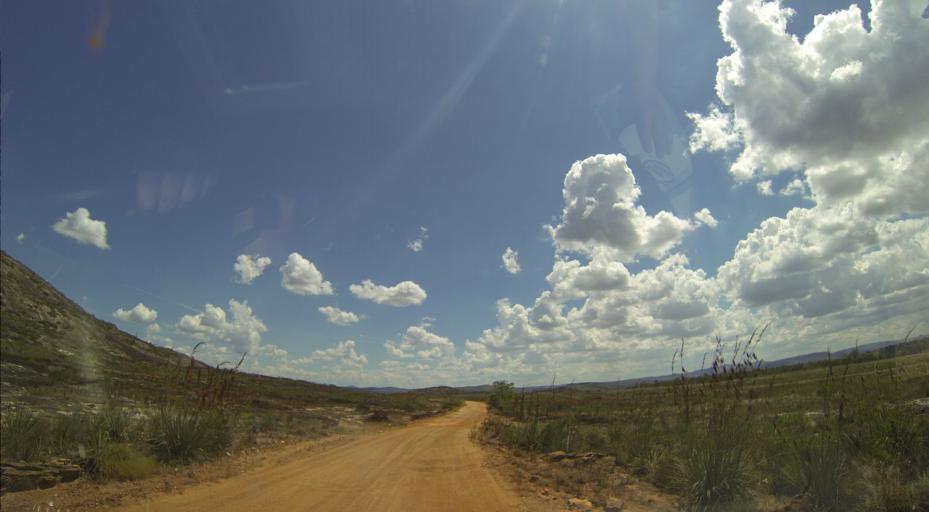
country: BR
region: Minas Gerais
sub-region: Serro
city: Serro
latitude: -18.4798
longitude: -43.4625
